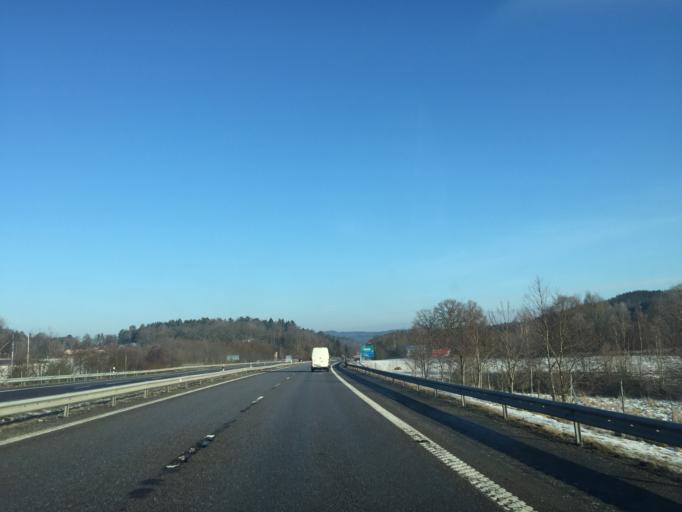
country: SE
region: Vaestra Goetaland
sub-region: Uddevalla Kommun
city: Ljungskile
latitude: 58.2003
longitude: 11.9081
